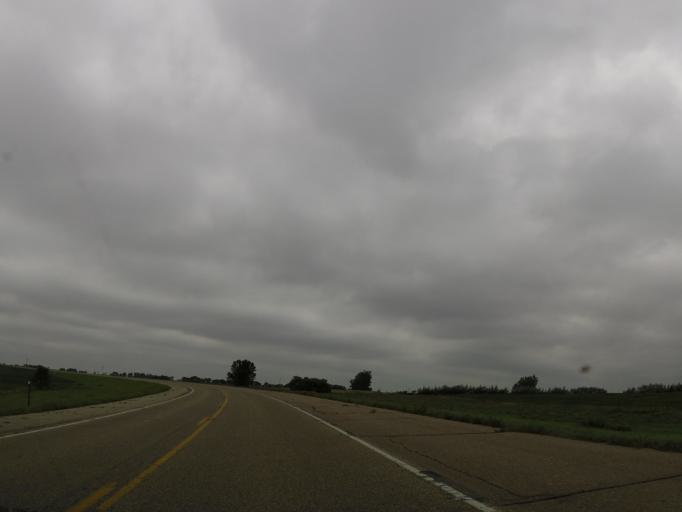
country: US
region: South Dakota
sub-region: Deuel County
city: Clear Lake
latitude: 44.9334
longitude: -96.6733
